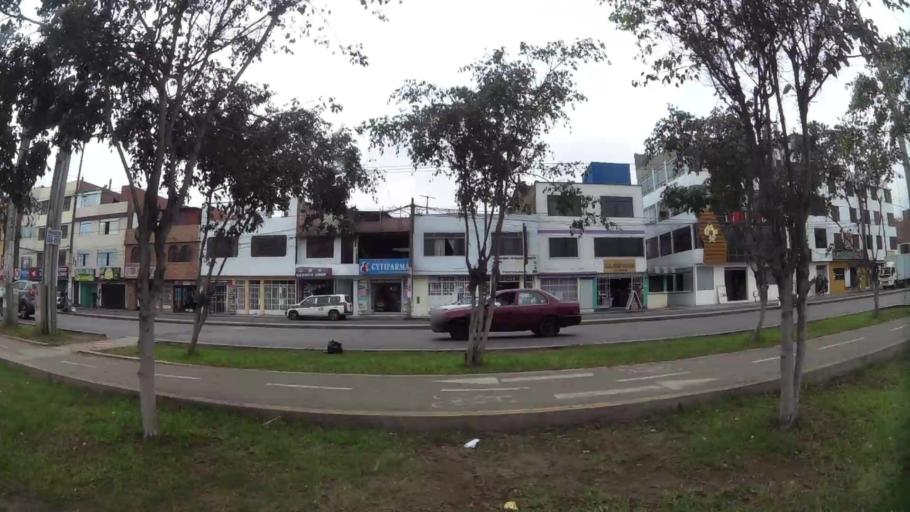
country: PE
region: Lima
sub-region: Lima
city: Independencia
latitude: -11.9839
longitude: -77.0714
